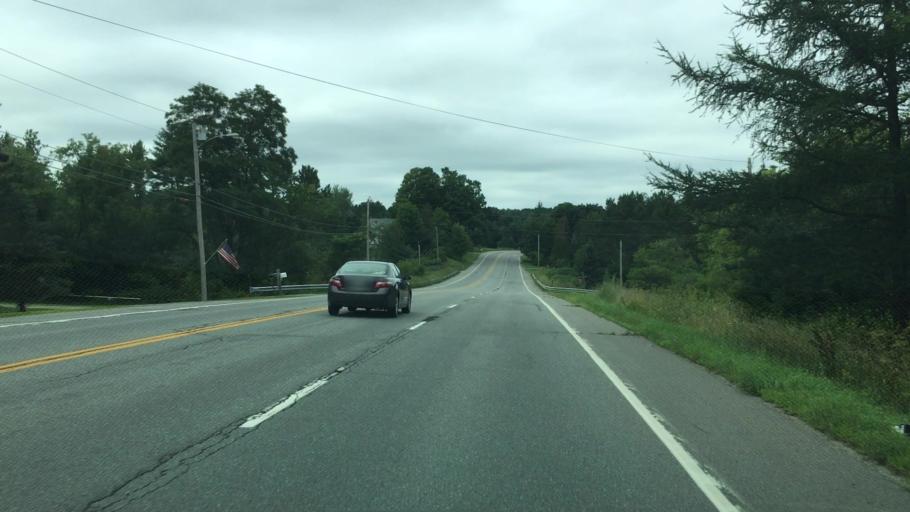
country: US
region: Maine
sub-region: Penobscot County
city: Orrington
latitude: 44.7084
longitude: -68.8470
